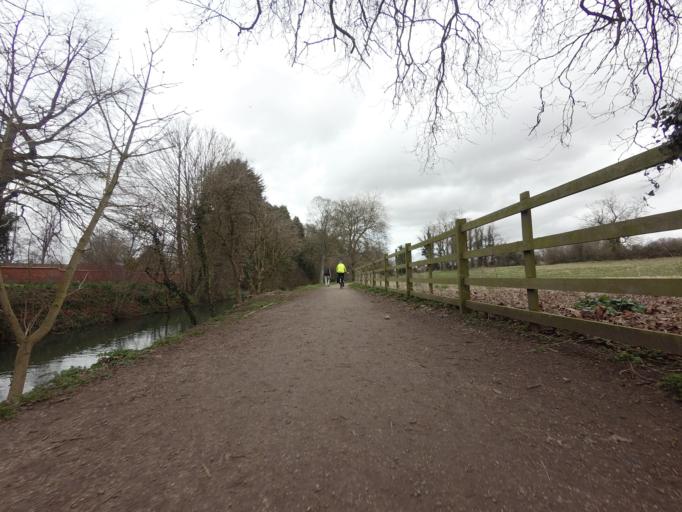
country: GB
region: England
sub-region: Lincolnshire
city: Grantham
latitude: 52.9146
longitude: -0.6383
